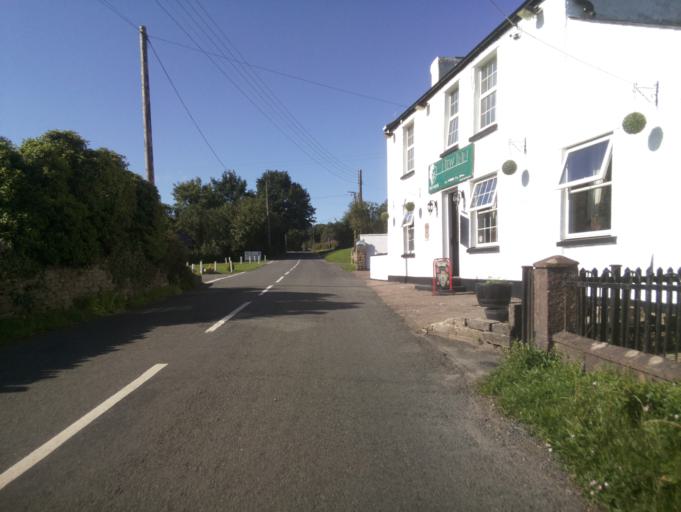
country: GB
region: England
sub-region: Gloucestershire
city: Coleford
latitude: 51.8178
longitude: -2.6223
